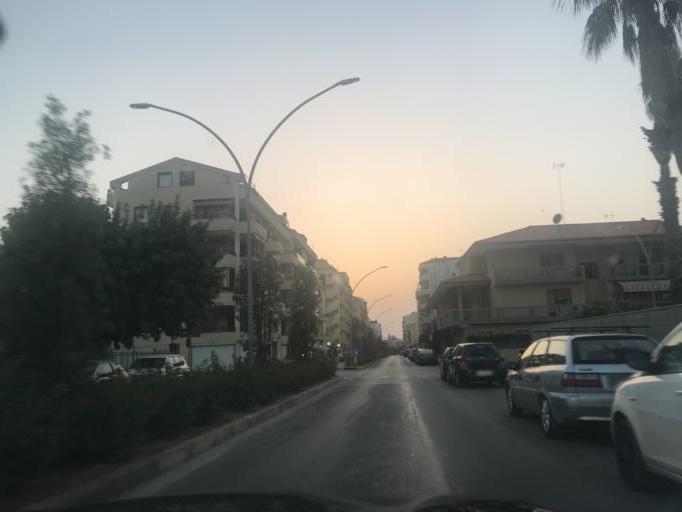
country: IT
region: Sardinia
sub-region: Provincia di Sassari
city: Alghero
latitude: 40.5527
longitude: 8.3246
